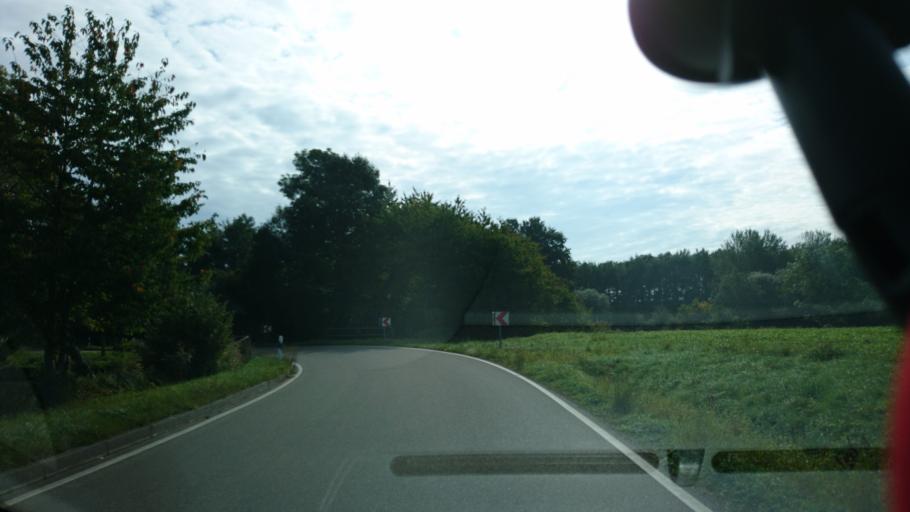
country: DE
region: Baden-Wuerttemberg
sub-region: Regierungsbezirk Stuttgart
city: Mainhardt
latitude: 49.0871
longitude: 9.6051
